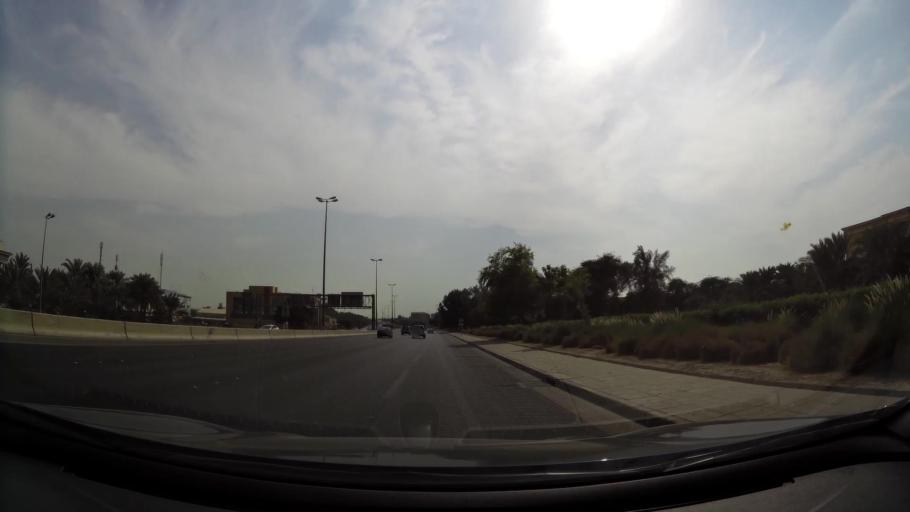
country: KW
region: Al Asimah
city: Ash Shamiyah
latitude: 29.3532
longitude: 47.9730
